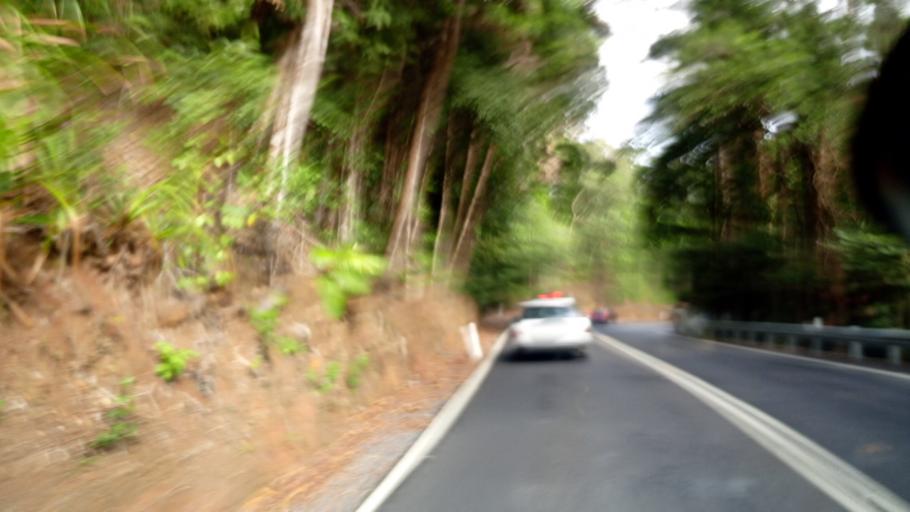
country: AU
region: Queensland
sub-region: Tablelands
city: Kuranda
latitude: -16.8291
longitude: 145.6584
